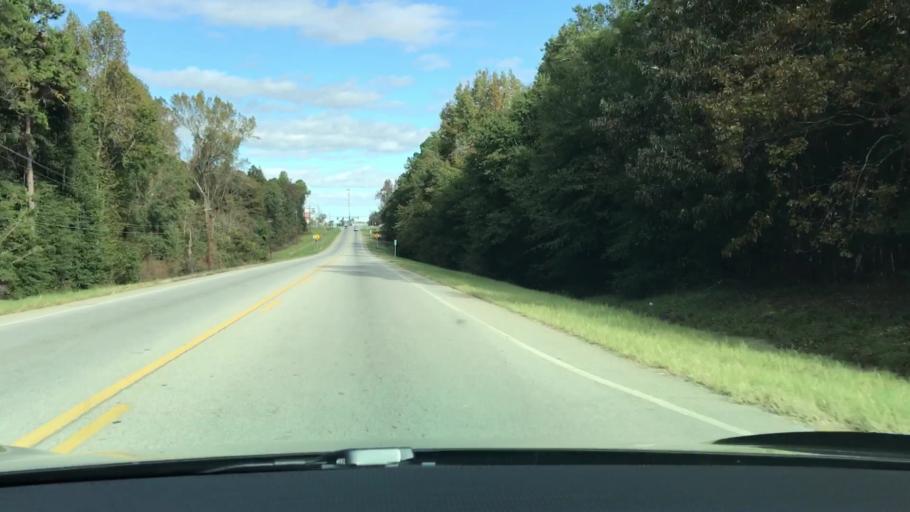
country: US
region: Georgia
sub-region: Jefferson County
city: Louisville
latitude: 33.0000
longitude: -82.3950
